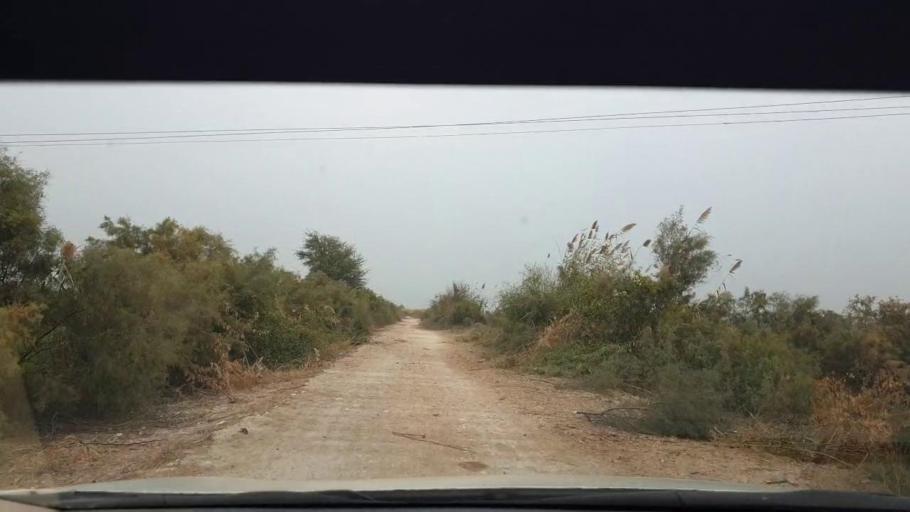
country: PK
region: Sindh
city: Berani
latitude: 25.8867
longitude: 68.7626
